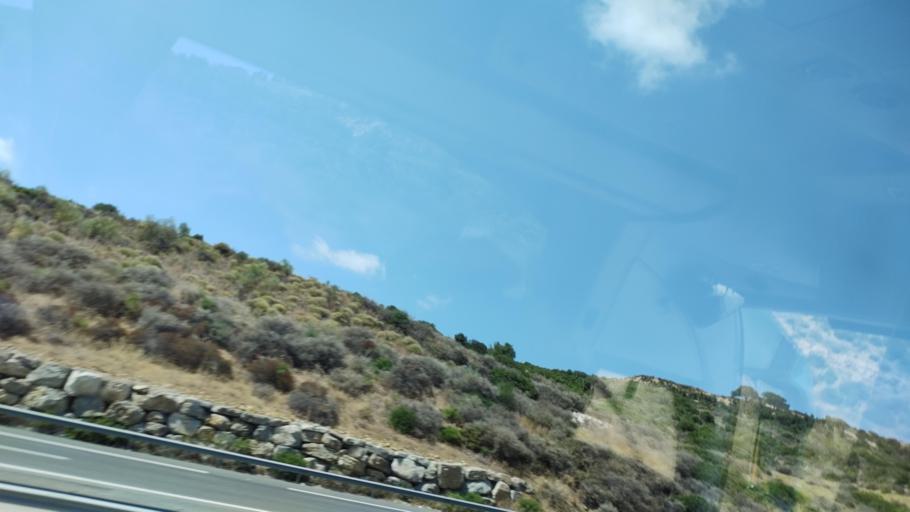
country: ES
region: Andalusia
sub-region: Provincia de Malaga
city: Manilva
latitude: 36.4009
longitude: -5.2464
